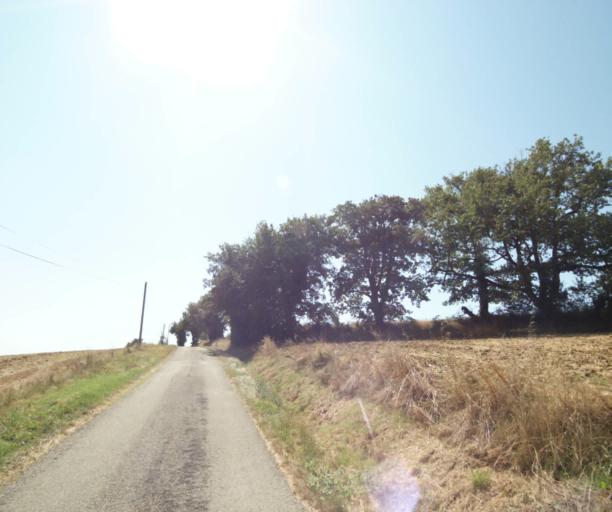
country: FR
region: Midi-Pyrenees
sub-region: Departement de l'Ariege
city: Lezat-sur-Leze
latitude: 43.2641
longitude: 1.3817
